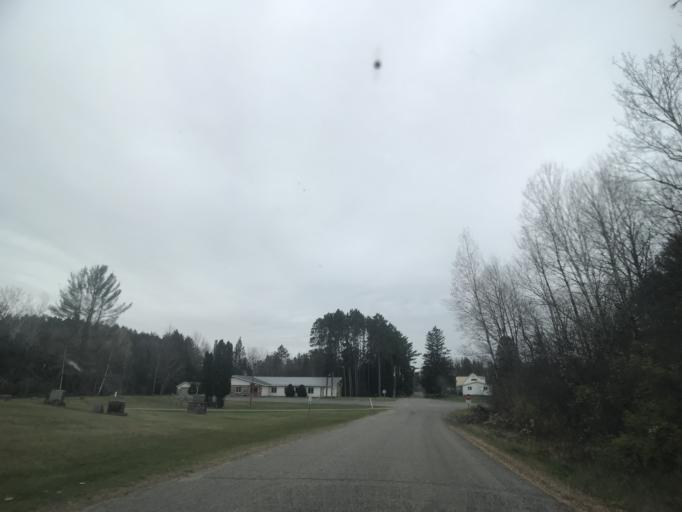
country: US
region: Wisconsin
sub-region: Menominee County
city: Legend Lake
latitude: 45.1810
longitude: -88.4673
